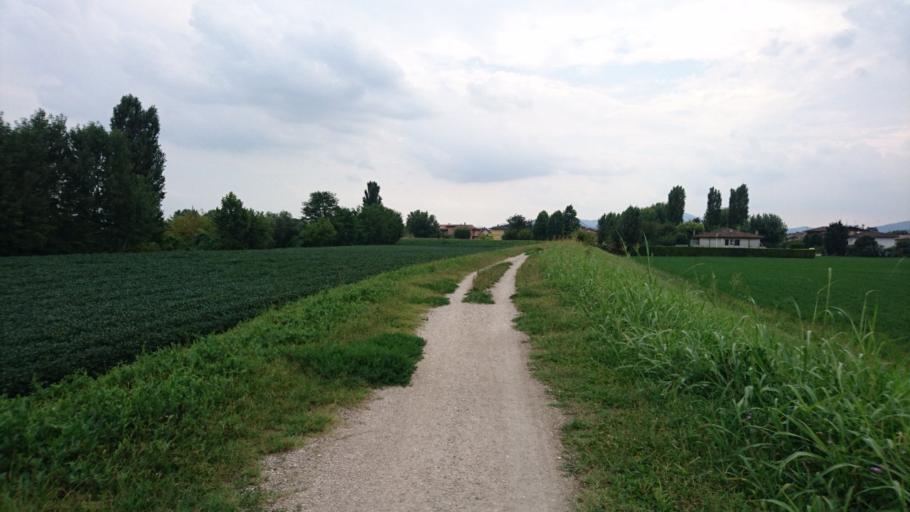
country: IT
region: Veneto
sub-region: Provincia di Padova
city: Saccolongo
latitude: 45.4106
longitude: 11.7428
